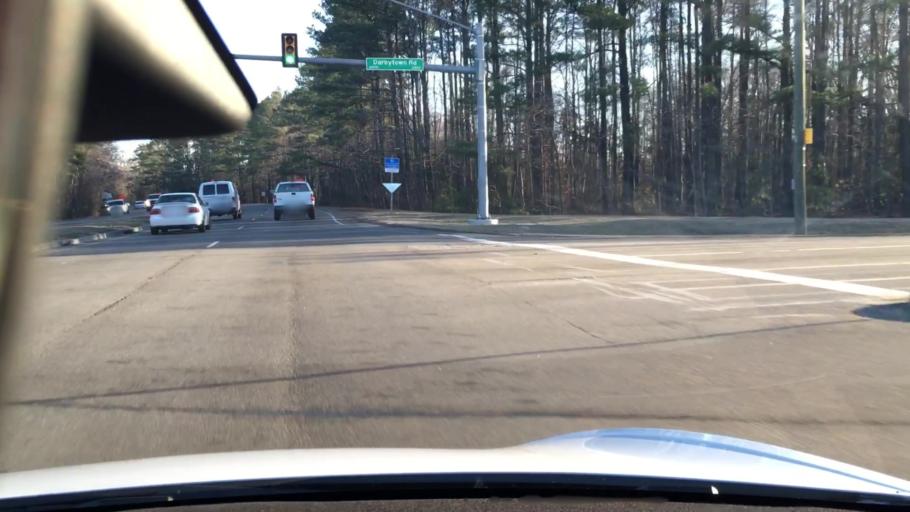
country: US
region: Virginia
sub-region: Henrico County
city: Fort Lee
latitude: 37.4828
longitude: -77.3572
